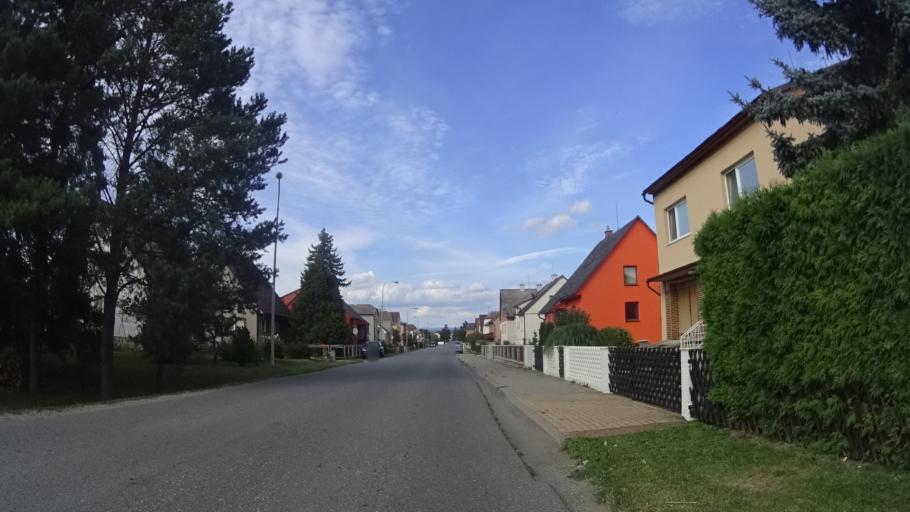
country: CZ
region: Olomoucky
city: Moravicany
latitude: 49.7904
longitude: 16.9635
